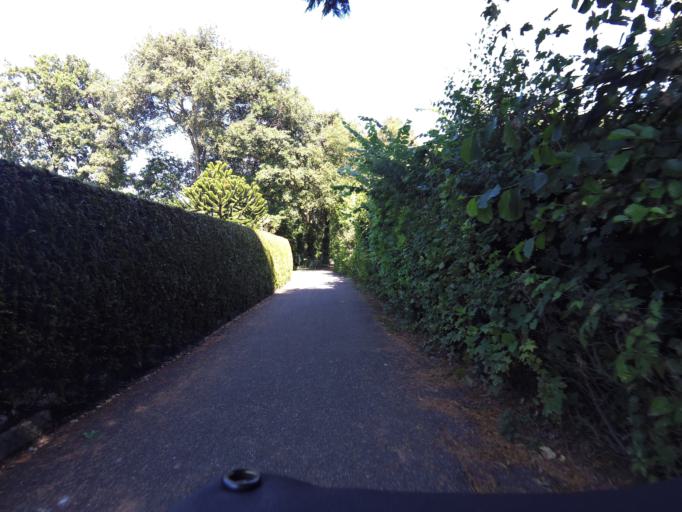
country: NL
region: Zeeland
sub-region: Schouwen-Duiveland
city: Renesse
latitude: 51.7276
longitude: 3.7530
